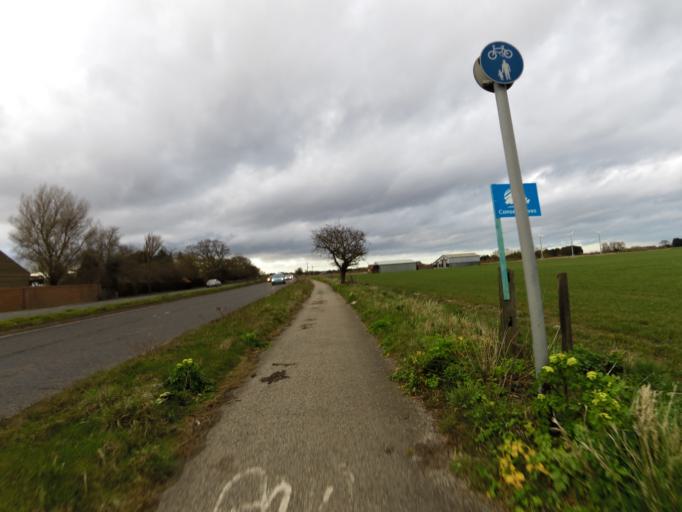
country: GB
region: England
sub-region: Norfolk
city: Hopton on Sea
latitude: 52.5510
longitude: 1.7184
